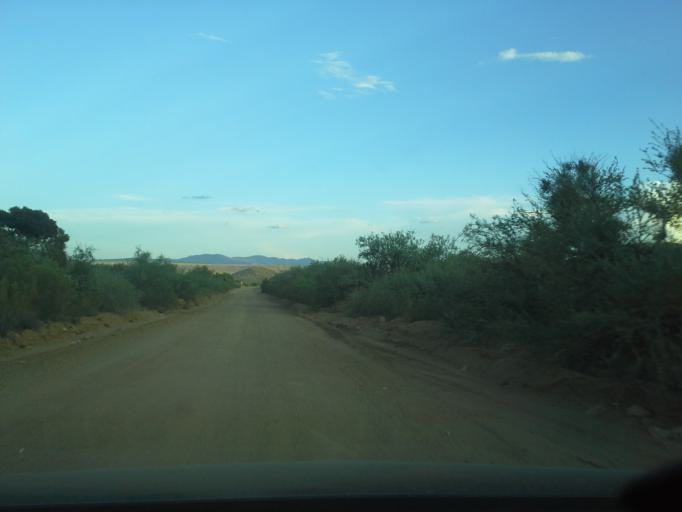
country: US
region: Arizona
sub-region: Yavapai County
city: Spring Valley
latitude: 34.2588
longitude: -112.1785
